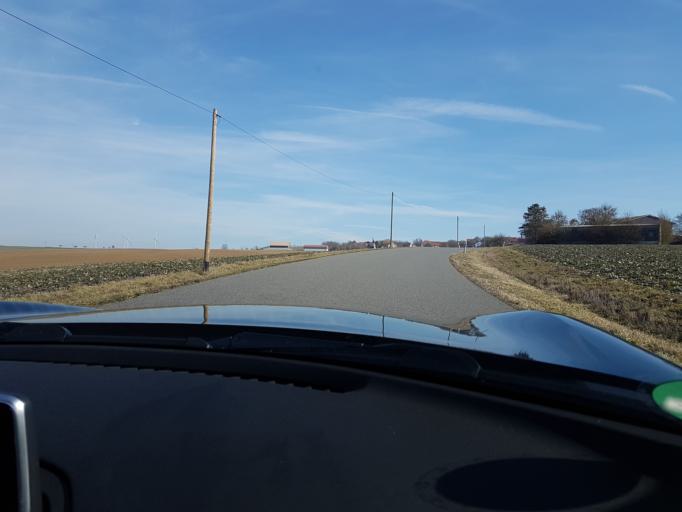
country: DE
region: Baden-Wuerttemberg
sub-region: Karlsruhe Region
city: Rosenberg
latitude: 49.4434
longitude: 9.4733
